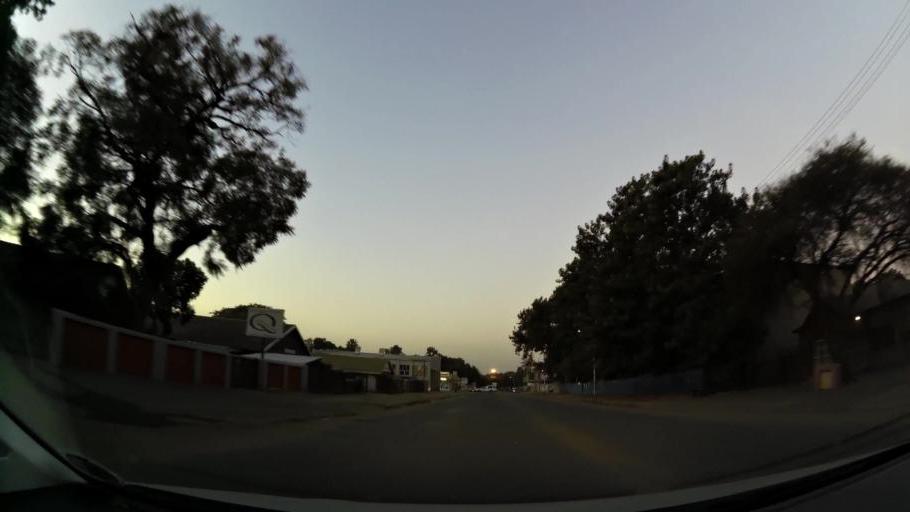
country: ZA
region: North-West
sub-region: Bojanala Platinum District Municipality
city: Rustenburg
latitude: -25.6680
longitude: 27.2499
